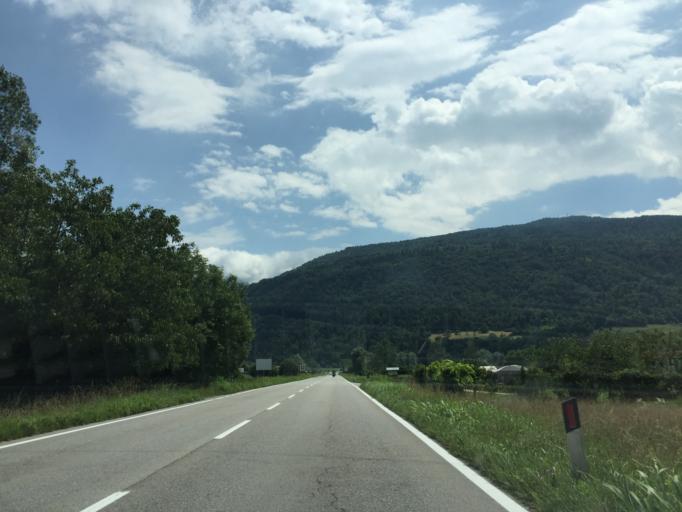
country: IT
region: Veneto
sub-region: Provincia di Belluno
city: Fonzaso
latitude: 46.0074
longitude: 11.7997
